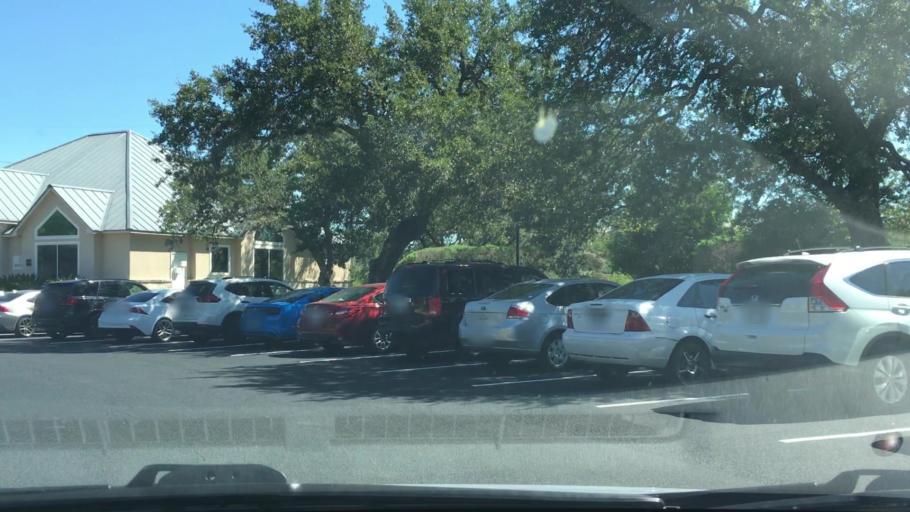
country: US
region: Texas
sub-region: Bexar County
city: Shavano Park
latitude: 29.5819
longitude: -98.5392
